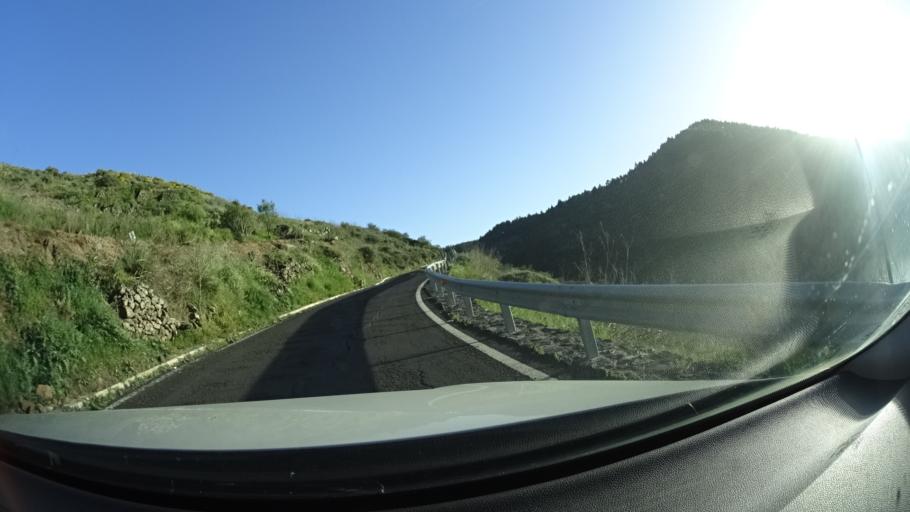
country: ES
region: Canary Islands
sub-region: Provincia de Las Palmas
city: Artenara
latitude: 28.0367
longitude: -15.6717
